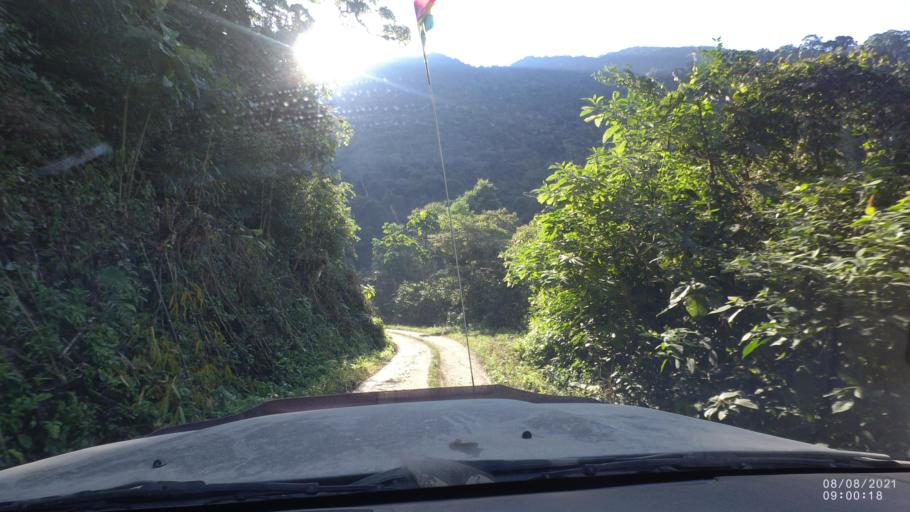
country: BO
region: La Paz
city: Quime
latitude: -16.5503
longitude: -66.7382
